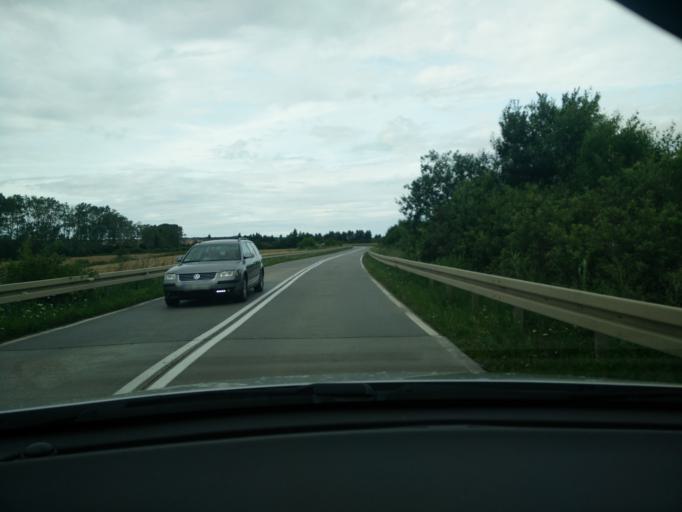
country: PL
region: Pomeranian Voivodeship
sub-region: Powiat pucki
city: Mrzezino
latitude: 54.6274
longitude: 18.4376
